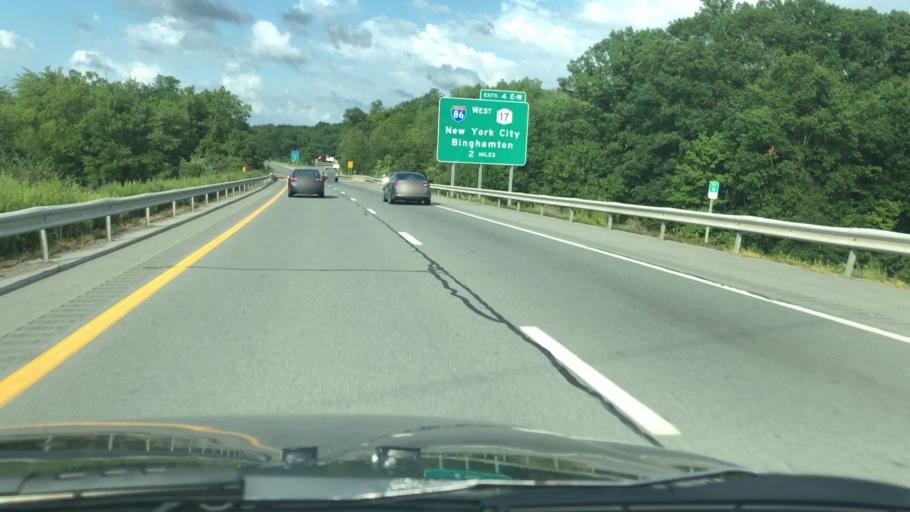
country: US
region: New York
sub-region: Orange County
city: Mechanicstown
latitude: 41.4222
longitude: -74.4014
